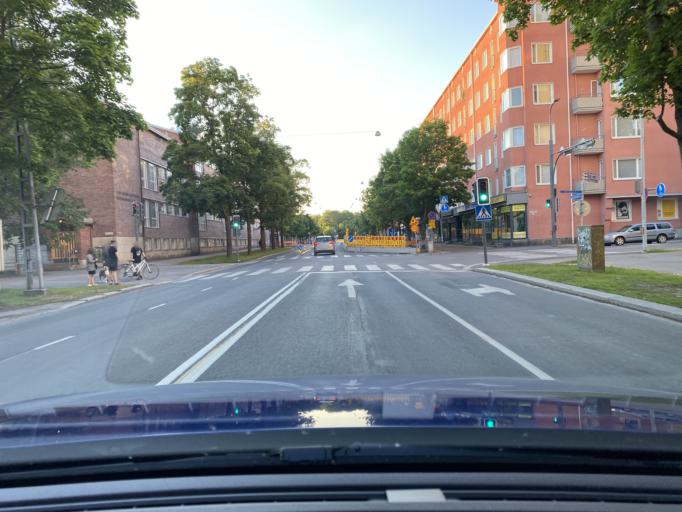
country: FI
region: Pirkanmaa
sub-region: Tampere
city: Tampere
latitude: 61.5007
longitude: 23.7870
